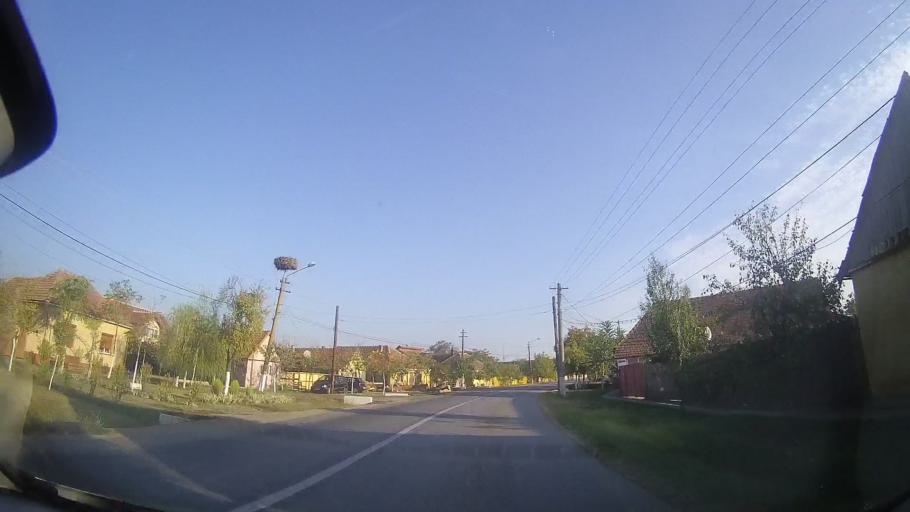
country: RO
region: Timis
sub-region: Comuna Fibis
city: Fibis
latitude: 45.9671
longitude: 21.4179
